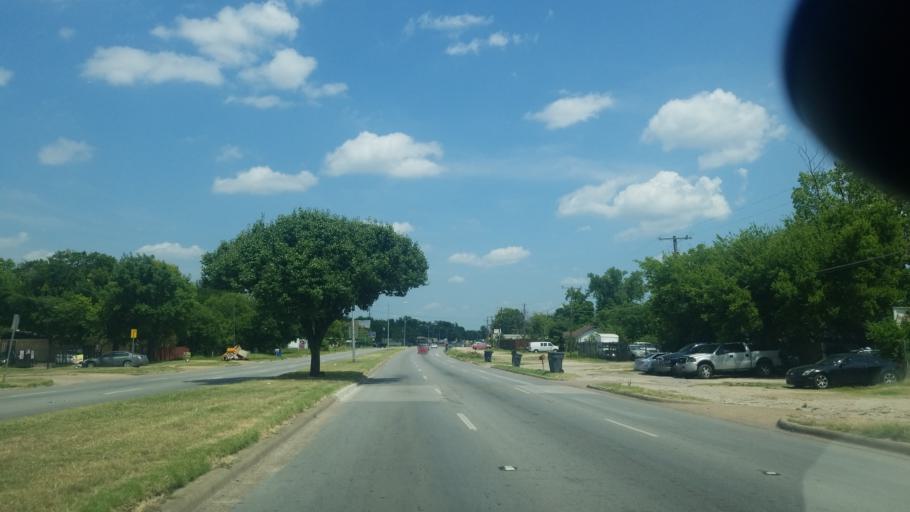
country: US
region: Texas
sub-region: Dallas County
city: Dallas
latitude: 32.7158
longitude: -96.7696
